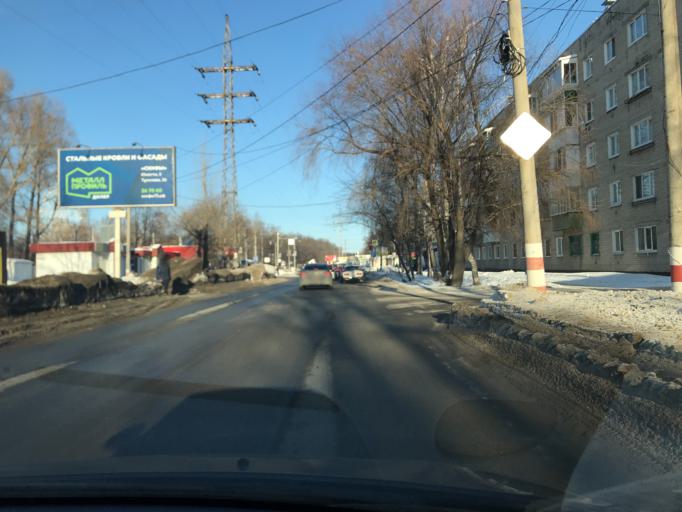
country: RU
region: Ulyanovsk
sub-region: Ulyanovskiy Rayon
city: Ulyanovsk
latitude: 54.3516
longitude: 48.3607
